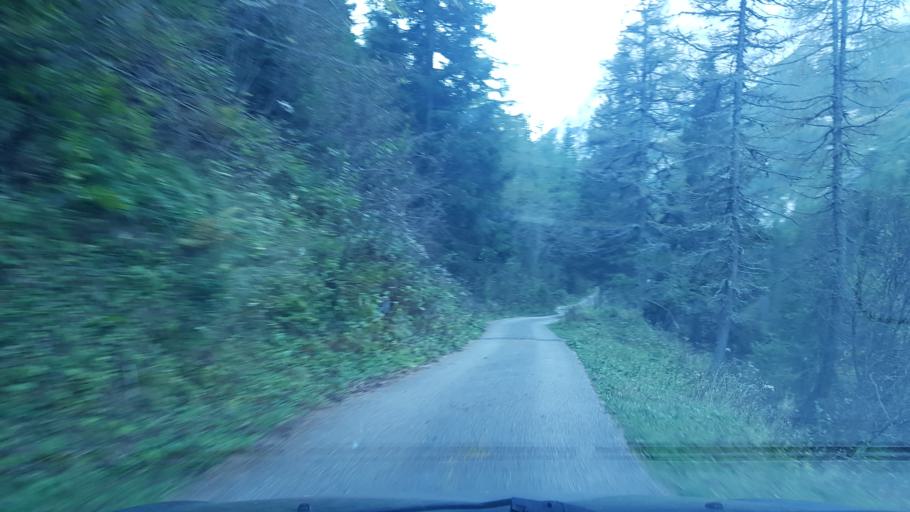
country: IT
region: Veneto
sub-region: Provincia di Belluno
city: Fusine
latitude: 46.3592
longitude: 12.0914
